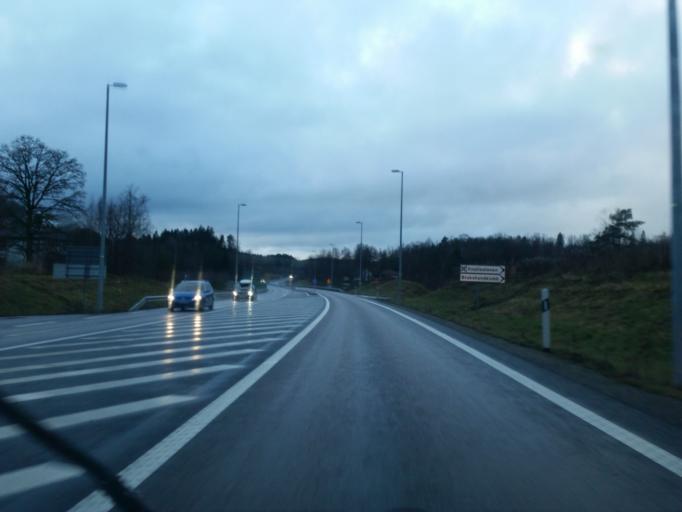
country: SE
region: Vaestra Goetaland
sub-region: Boras Kommun
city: Boras
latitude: 57.6803
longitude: 12.9642
